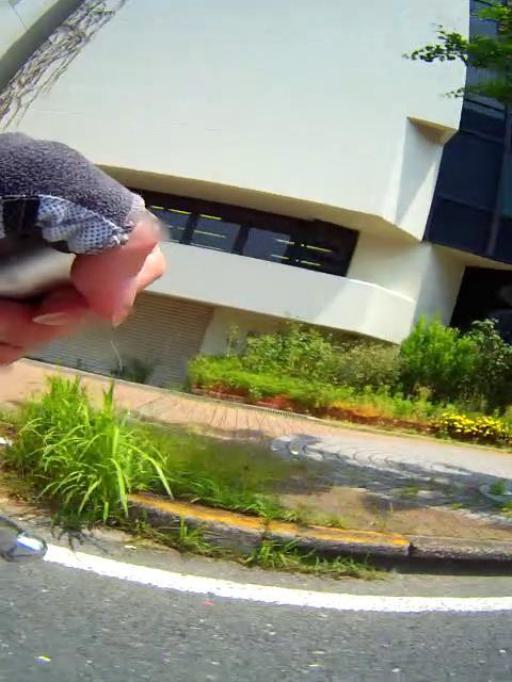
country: JP
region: Osaka
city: Mino
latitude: 34.8220
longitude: 135.4901
